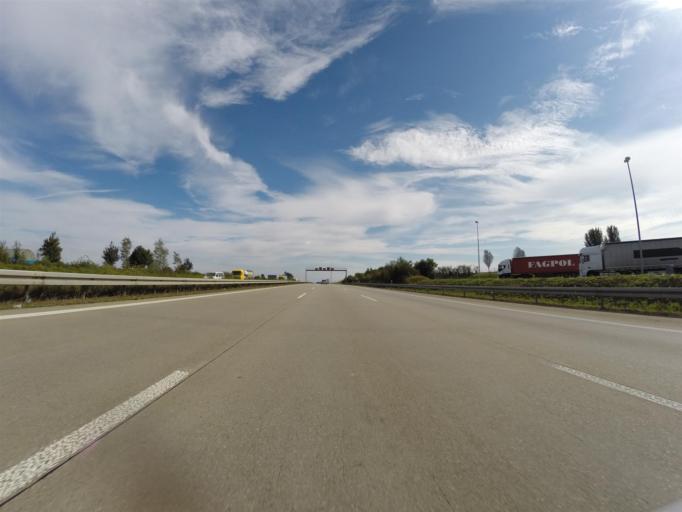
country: DE
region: Saxony
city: Wilsdruff
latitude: 51.0618
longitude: 13.5742
